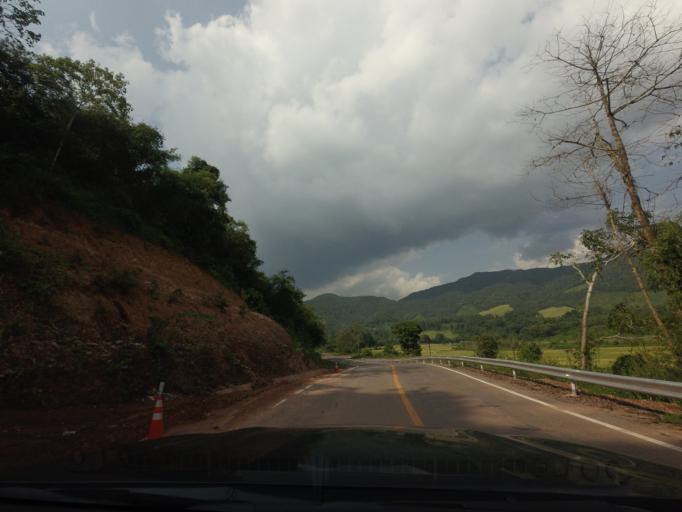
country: TH
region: Nan
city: Bo Kluea
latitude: 19.2249
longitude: 101.1823
